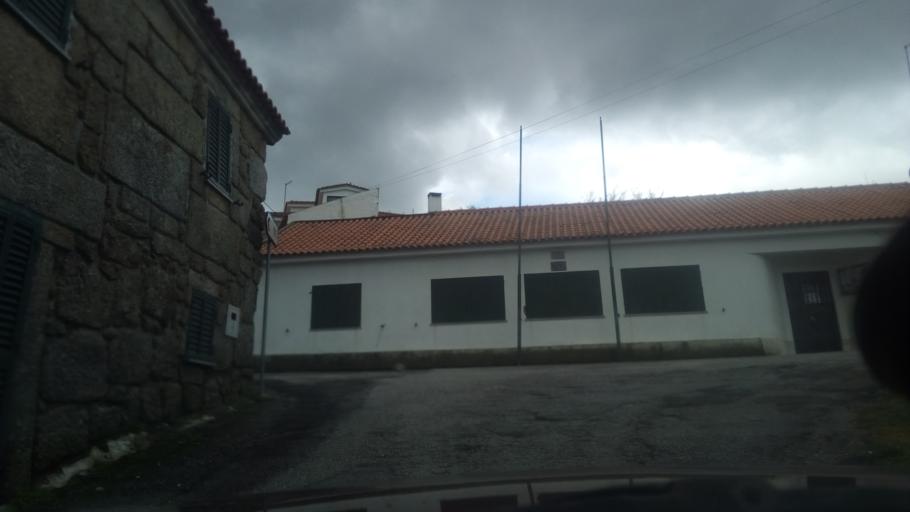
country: PT
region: Guarda
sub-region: Celorico da Beira
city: Celorico da Beira
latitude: 40.5570
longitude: -7.4570
